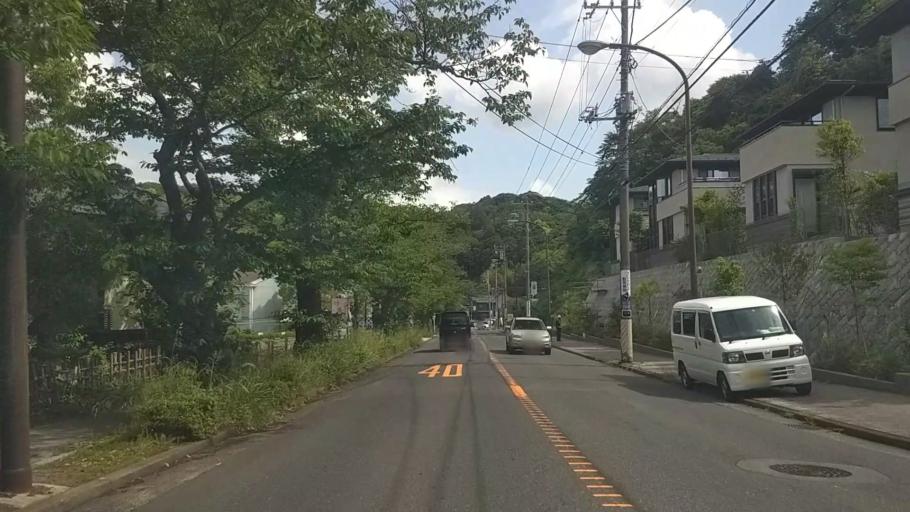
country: JP
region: Kanagawa
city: Zushi
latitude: 35.3178
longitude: 139.5769
